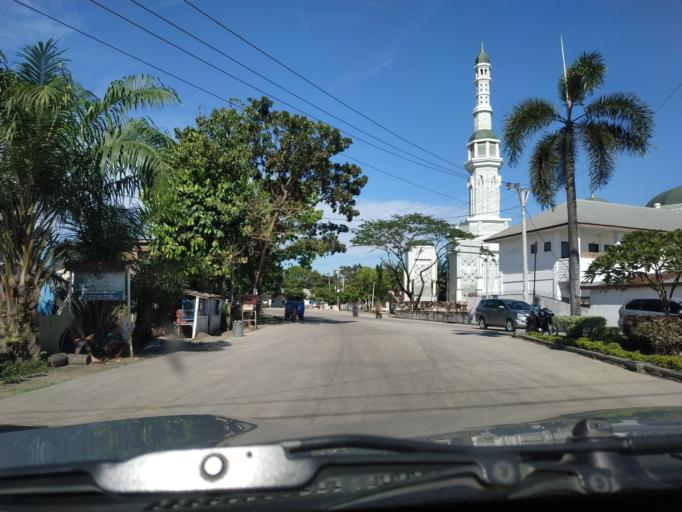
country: ID
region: North Sumatra
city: Tebingtinggi
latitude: 3.3533
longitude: 99.1667
